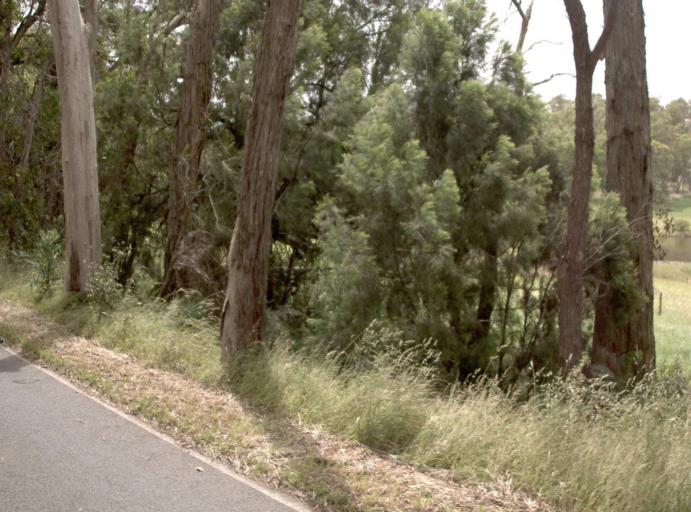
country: AU
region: Victoria
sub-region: Latrobe
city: Moe
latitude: -38.0767
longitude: 146.1700
